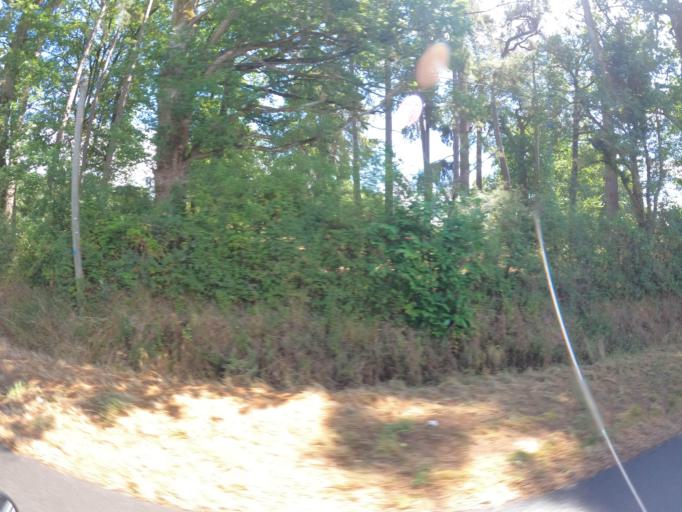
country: FR
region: Pays de la Loire
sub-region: Departement de Maine-et-Loire
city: Champigne
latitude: 47.6190
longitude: -0.5837
